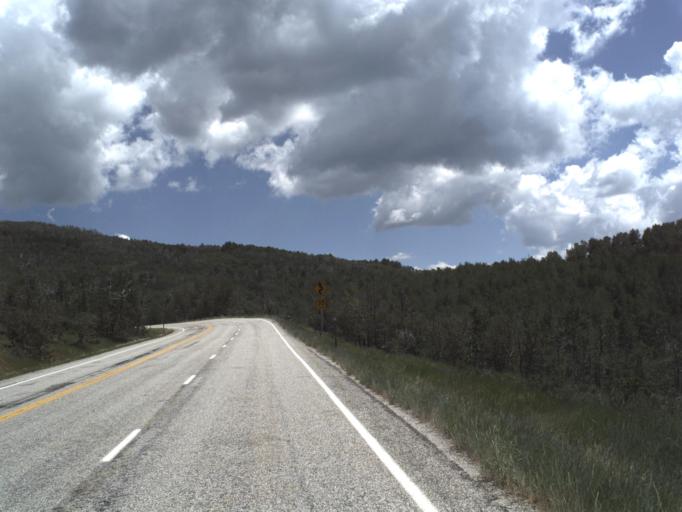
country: US
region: Utah
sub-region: Weber County
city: Wolf Creek
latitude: 41.4190
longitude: -111.5647
